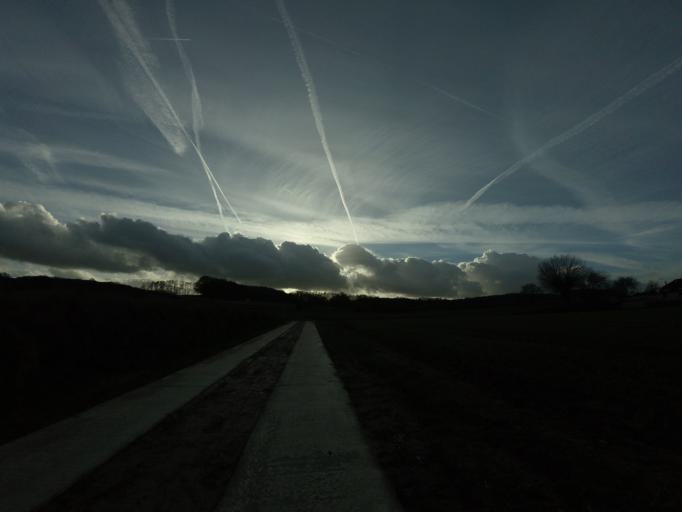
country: BE
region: Flanders
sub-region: Provincie Vlaams-Brabant
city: Kortenberg
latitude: 50.8716
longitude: 4.5711
